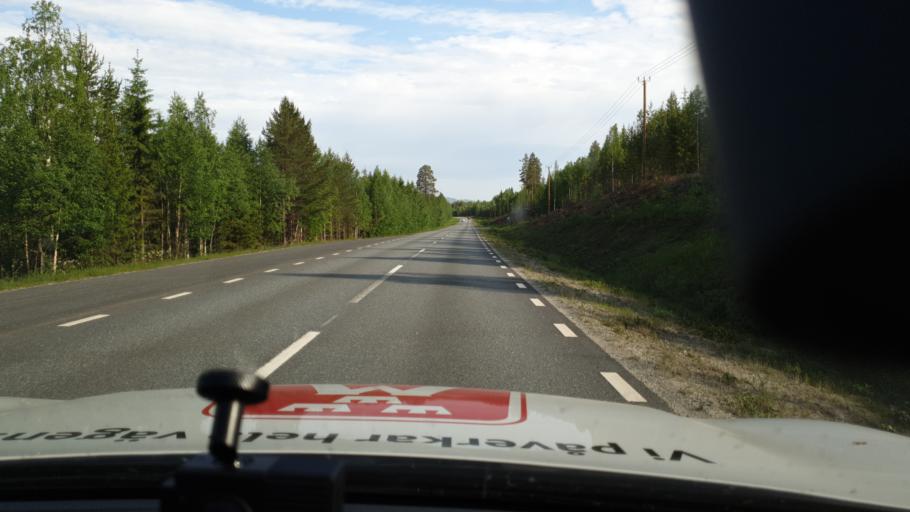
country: SE
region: Vaesterbotten
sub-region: Bjurholms Kommun
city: Bjurholm
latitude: 64.3257
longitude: 19.1555
